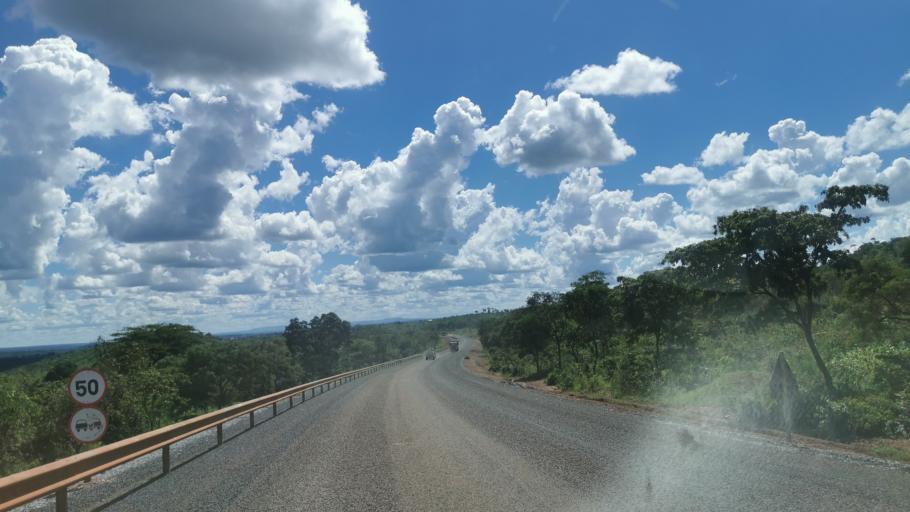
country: TZ
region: Kigoma
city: Kakonko
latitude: -3.0090
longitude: 31.2277
